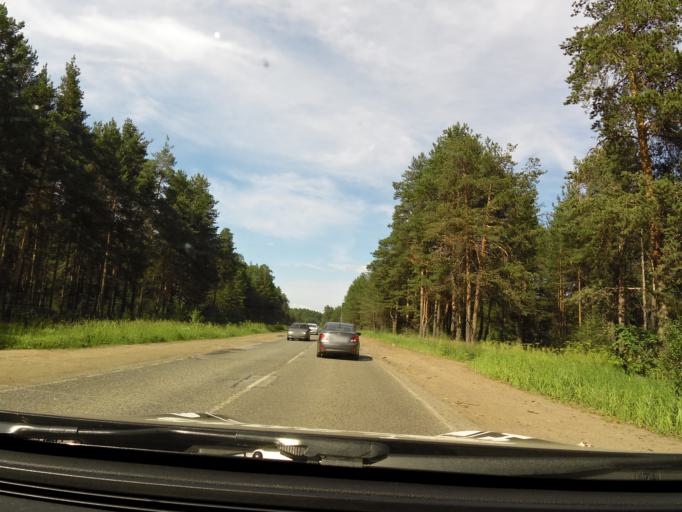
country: RU
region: Kirov
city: Belaya Kholunitsa
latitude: 58.8547
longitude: 50.8385
